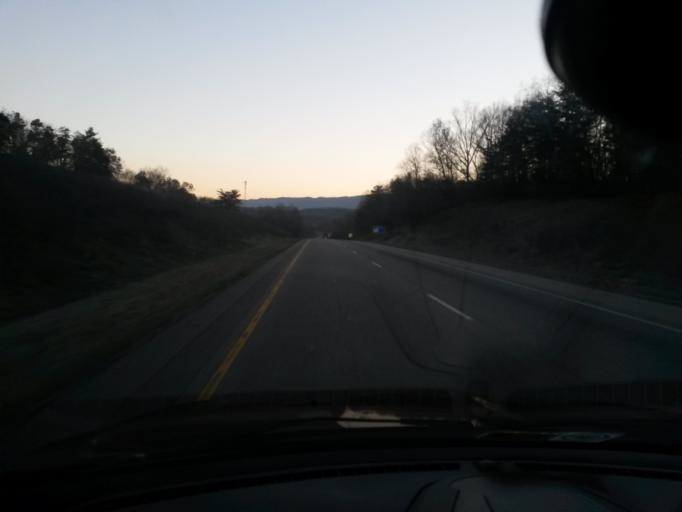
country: US
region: Virginia
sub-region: Alleghany County
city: Clifton Forge
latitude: 37.8291
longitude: -79.7757
